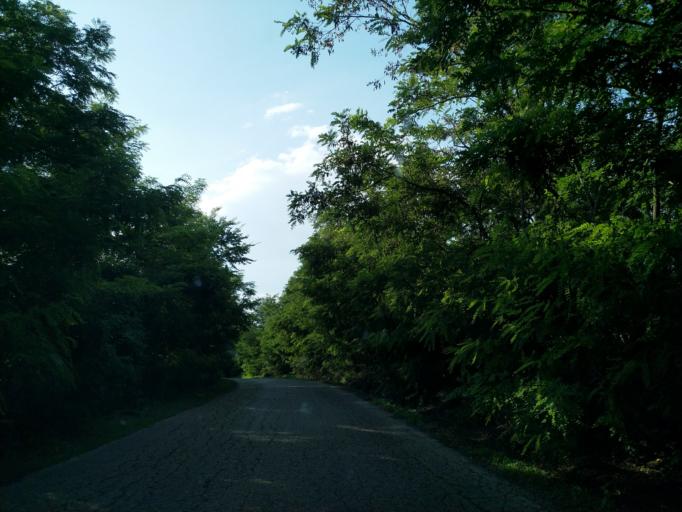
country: RS
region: Central Serbia
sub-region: Pomoravski Okrug
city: Jagodina
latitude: 43.9970
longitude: 21.1926
